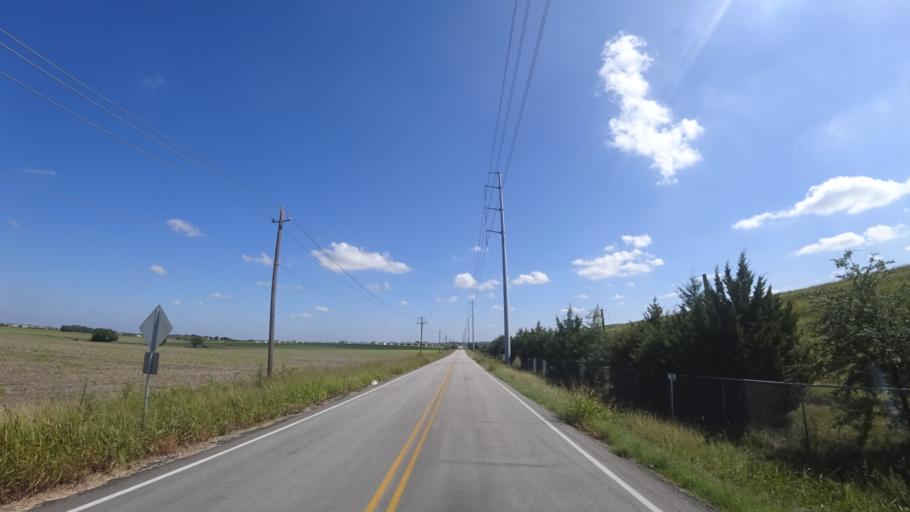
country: US
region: Texas
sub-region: Travis County
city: Manor
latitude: 30.3495
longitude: -97.6295
